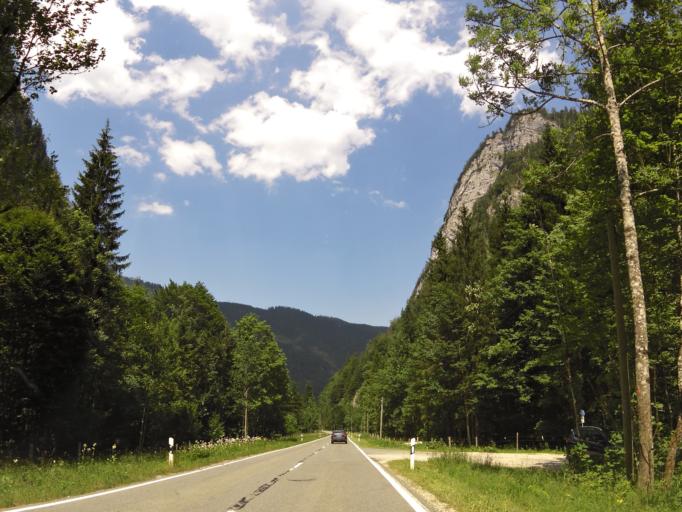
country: DE
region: Bavaria
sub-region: Upper Bavaria
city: Ruhpolding
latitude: 47.7015
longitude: 12.6154
